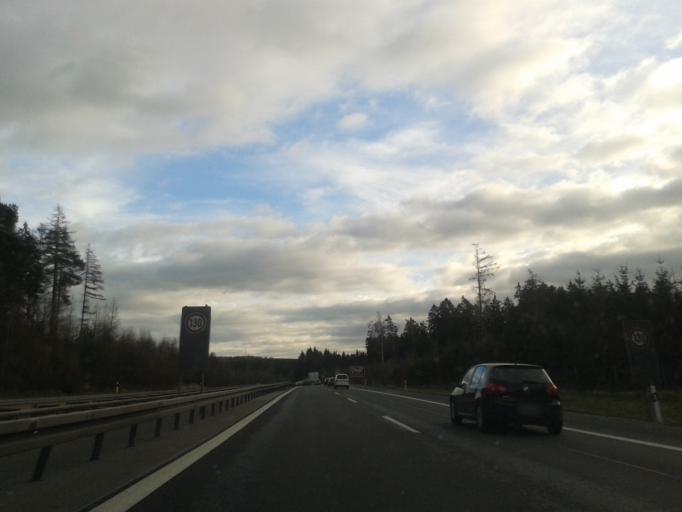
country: DE
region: Saxony
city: Hauswalde
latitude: 51.1751
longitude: 14.1058
